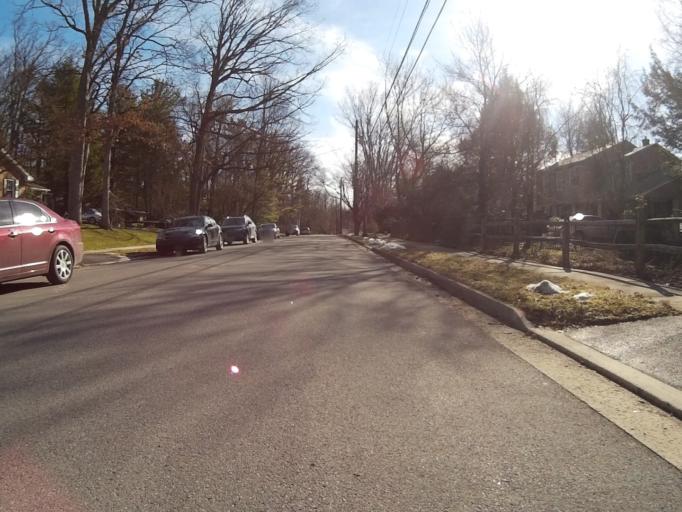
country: US
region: Pennsylvania
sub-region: Centre County
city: State College
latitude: 40.7978
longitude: -77.8818
